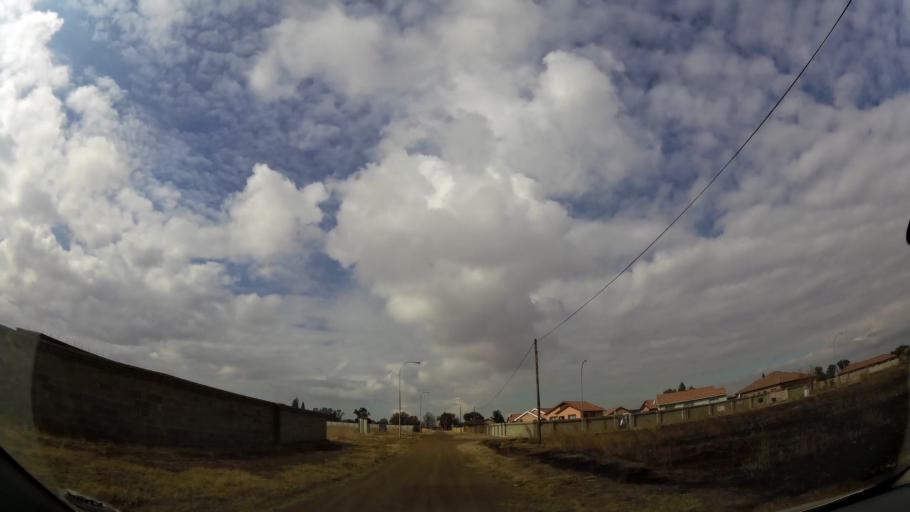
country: ZA
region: Gauteng
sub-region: Sedibeng District Municipality
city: Meyerton
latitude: -26.6026
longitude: 28.0504
